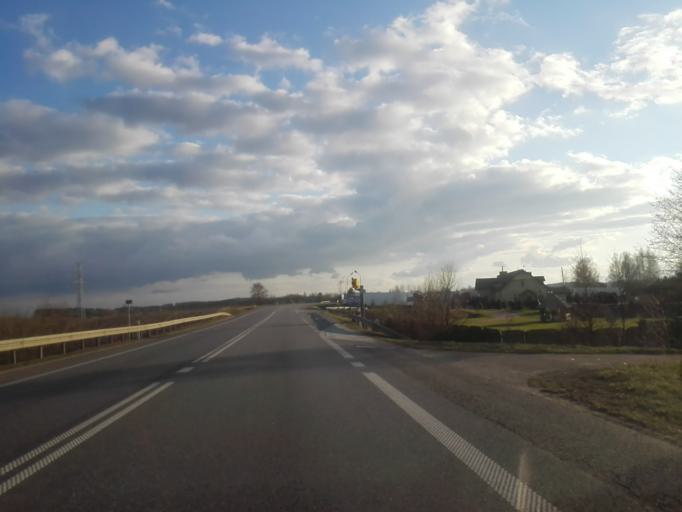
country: PL
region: Podlasie
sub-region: Suwalki
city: Suwalki
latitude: 54.1796
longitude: 22.9987
